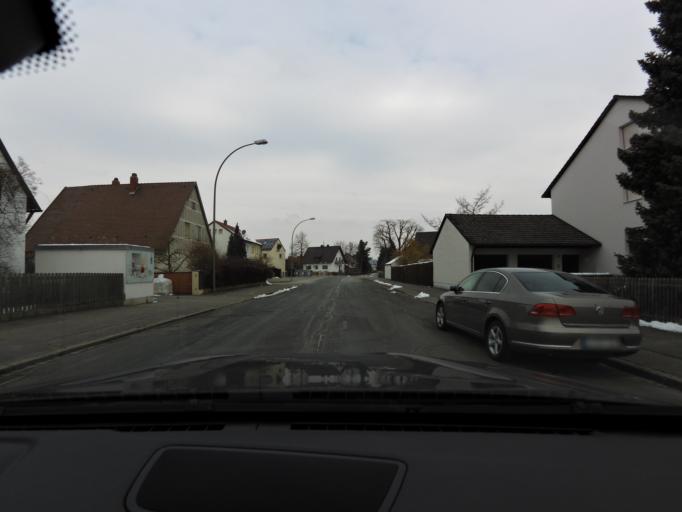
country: DE
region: Bavaria
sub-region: Lower Bavaria
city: Landshut
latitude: 48.5521
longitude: 12.1223
